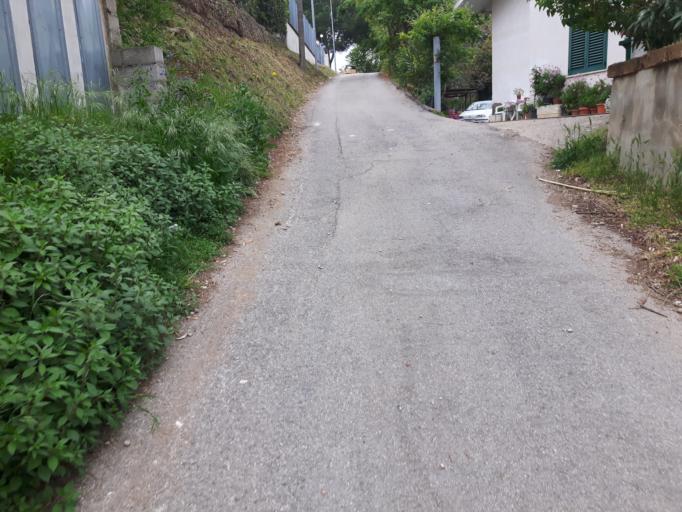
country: IT
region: Abruzzo
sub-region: Provincia di Chieti
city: Vasto
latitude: 42.1425
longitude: 14.6945
